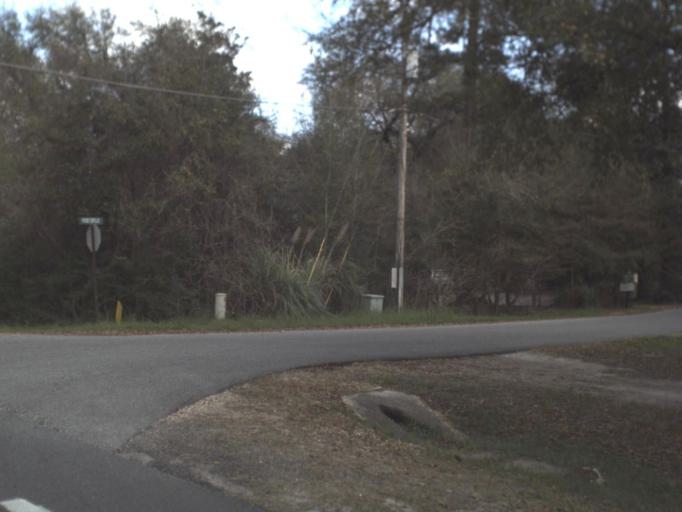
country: US
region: Florida
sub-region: Wakulla County
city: Crawfordville
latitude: 30.2831
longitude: -84.3538
